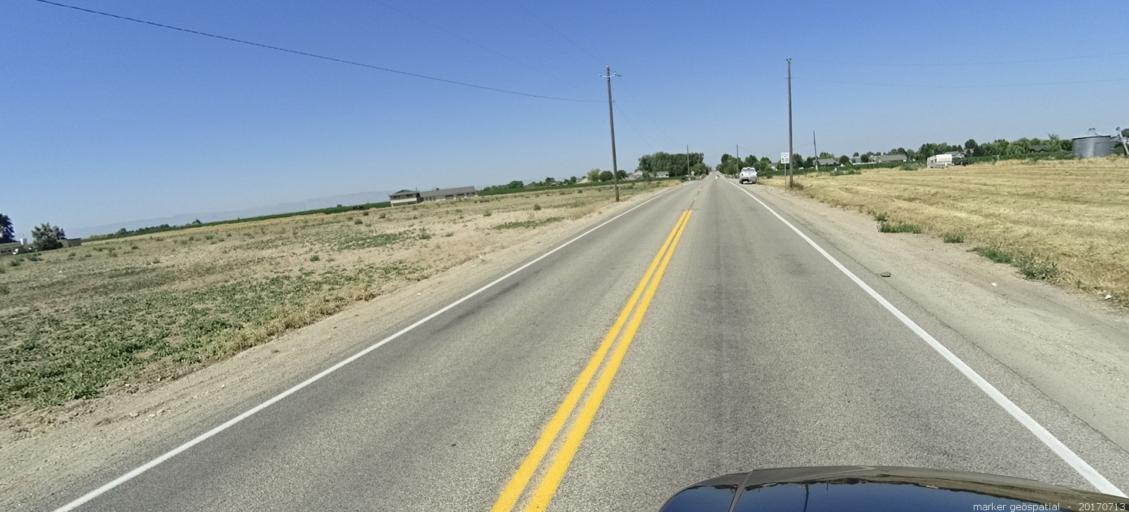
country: US
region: Idaho
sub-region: Ada County
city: Kuna
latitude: 43.5321
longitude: -116.4146
